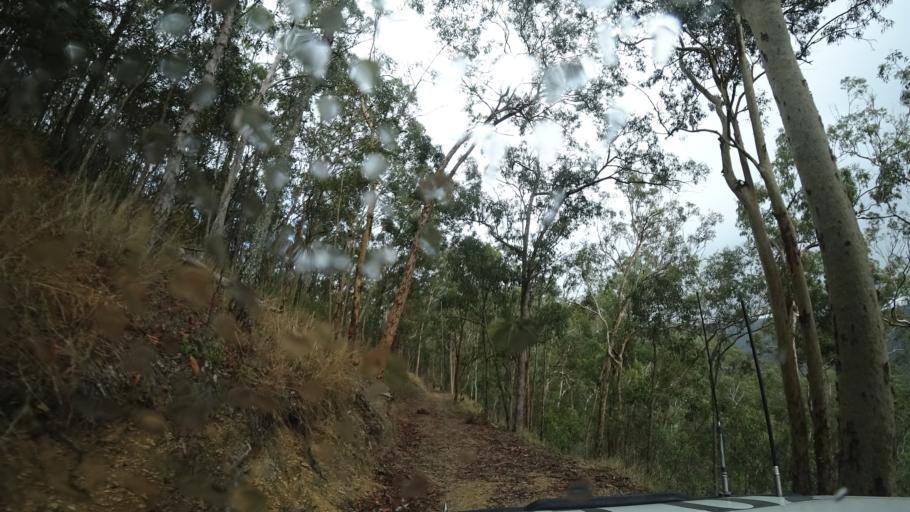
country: AU
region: Queensland
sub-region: Brisbane
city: Pullenvale
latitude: -27.4611
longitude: 152.8507
